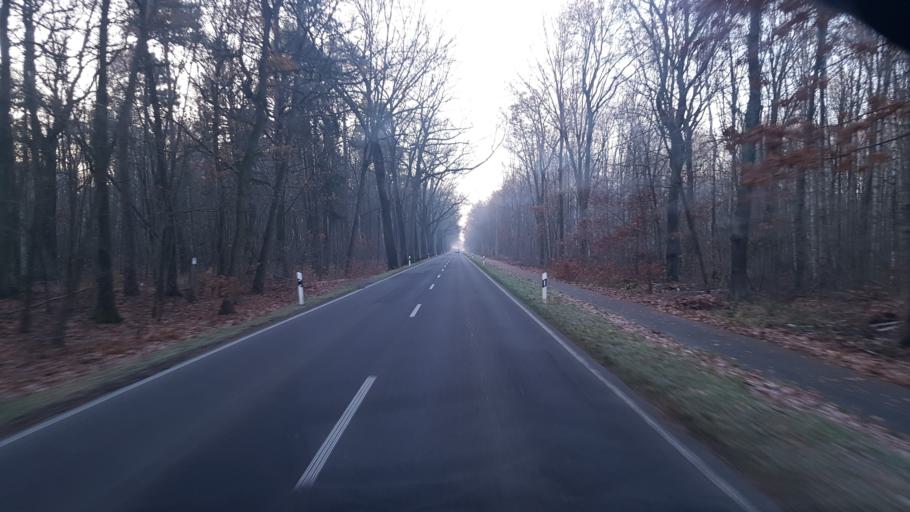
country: DE
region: Brandenburg
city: Tettau
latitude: 51.4444
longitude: 13.7346
